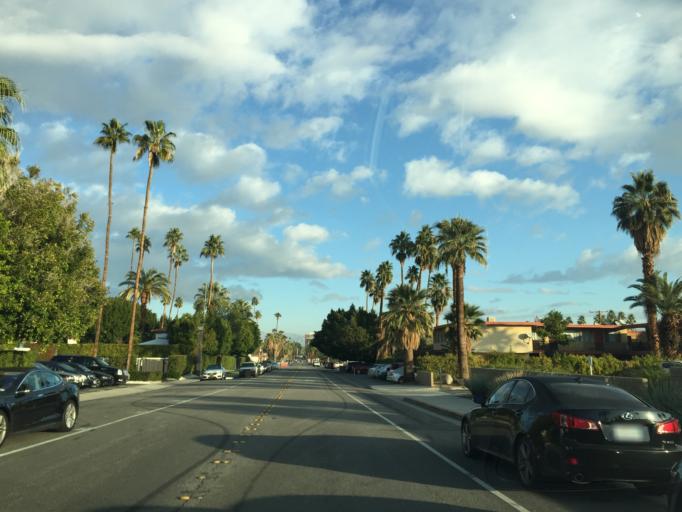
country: US
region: California
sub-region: Riverside County
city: Palm Springs
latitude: 33.8174
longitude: -116.5479
